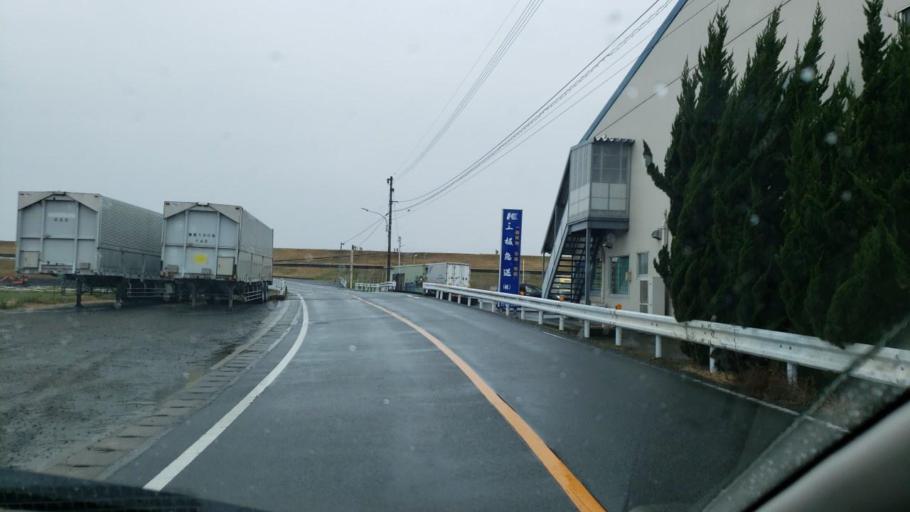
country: JP
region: Tokushima
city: Ishii
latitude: 34.0984
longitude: 134.4077
